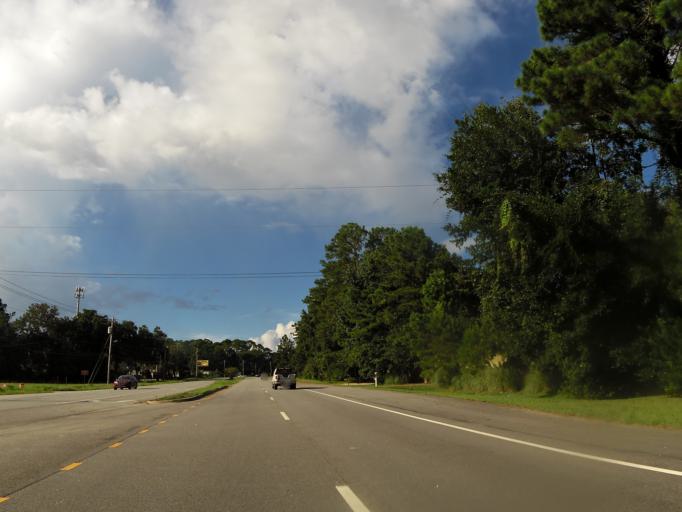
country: US
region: Georgia
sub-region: Glynn County
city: Country Club Estates
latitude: 31.2113
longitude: -81.4662
